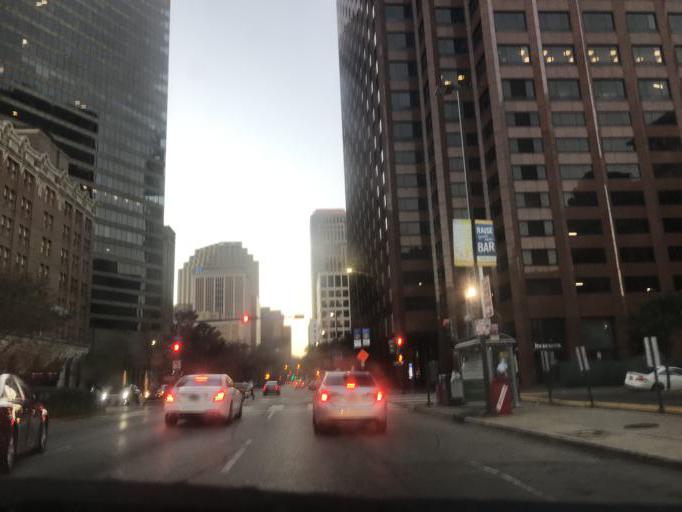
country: US
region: Louisiana
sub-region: Orleans Parish
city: New Orleans
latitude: 29.9493
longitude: -90.0690
